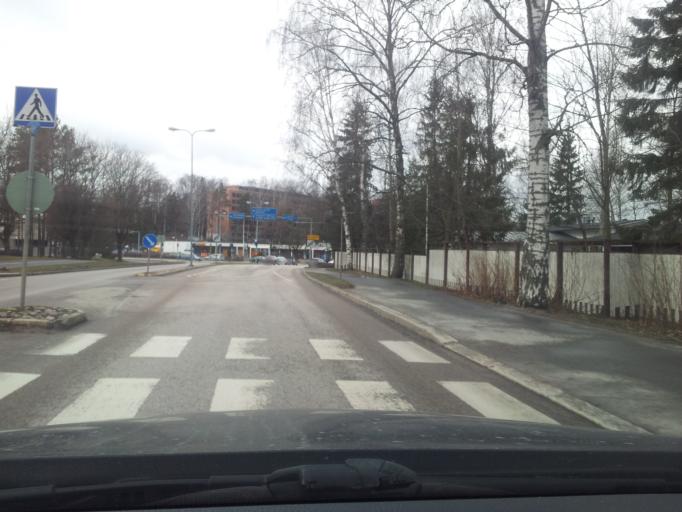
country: FI
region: Uusimaa
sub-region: Helsinki
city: Otaniemi
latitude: 60.1818
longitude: 24.7955
